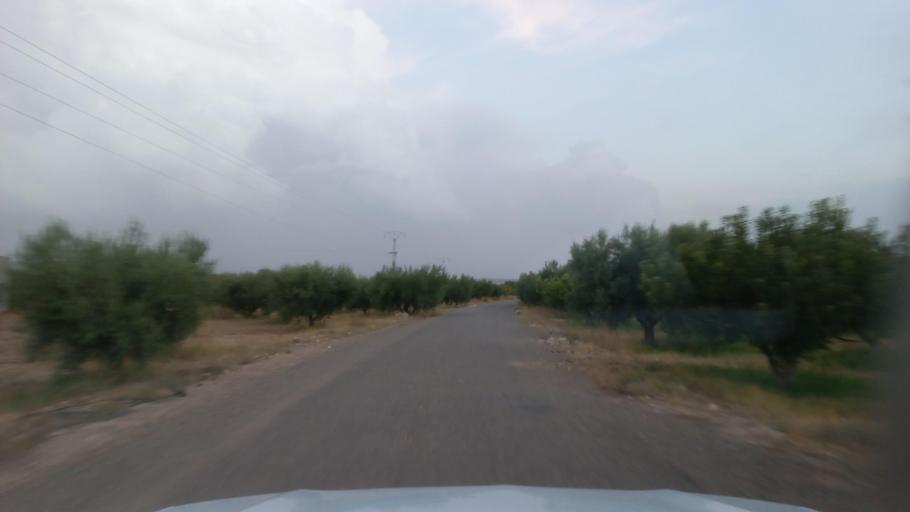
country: TN
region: Al Qasrayn
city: Kasserine
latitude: 35.2721
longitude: 9.0370
